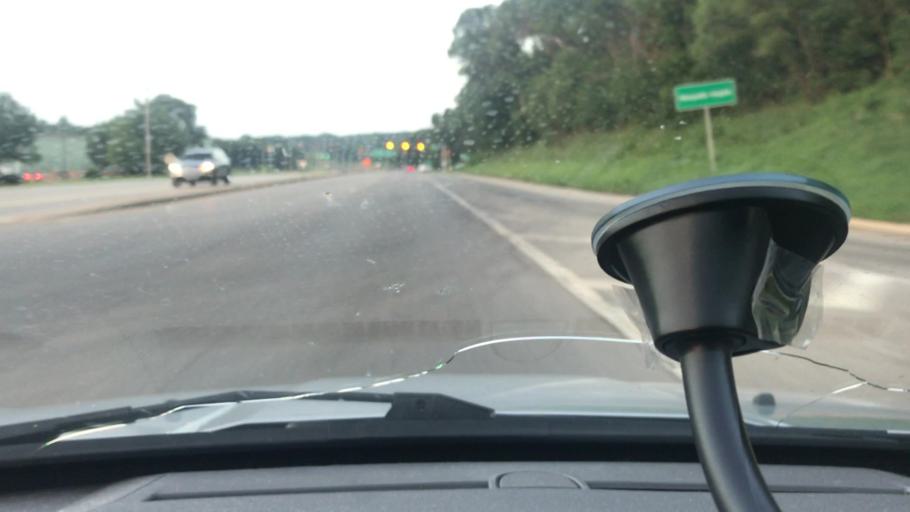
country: US
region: Illinois
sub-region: Tazewell County
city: North Pekin
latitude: 40.6254
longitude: -89.6187
